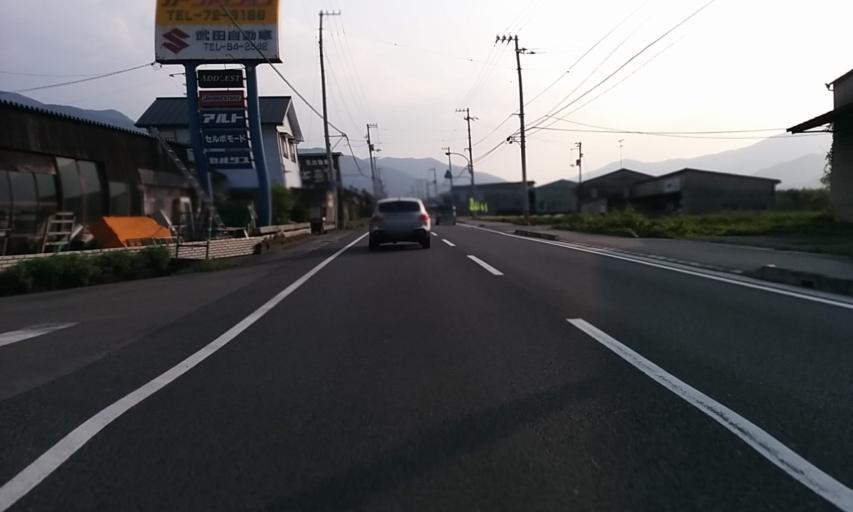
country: JP
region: Ehime
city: Saijo
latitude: 33.8754
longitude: 133.0627
